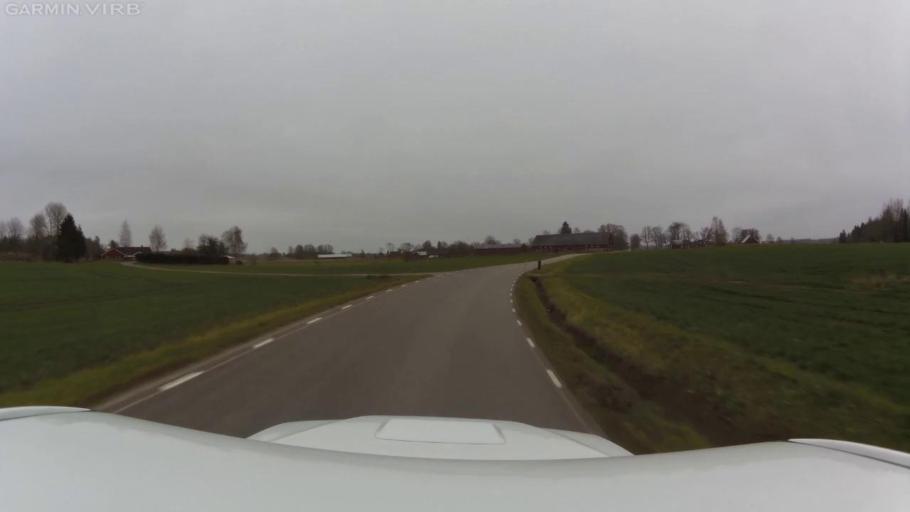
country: SE
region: OEstergoetland
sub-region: Linkopings Kommun
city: Vikingstad
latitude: 58.3112
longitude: 15.3787
